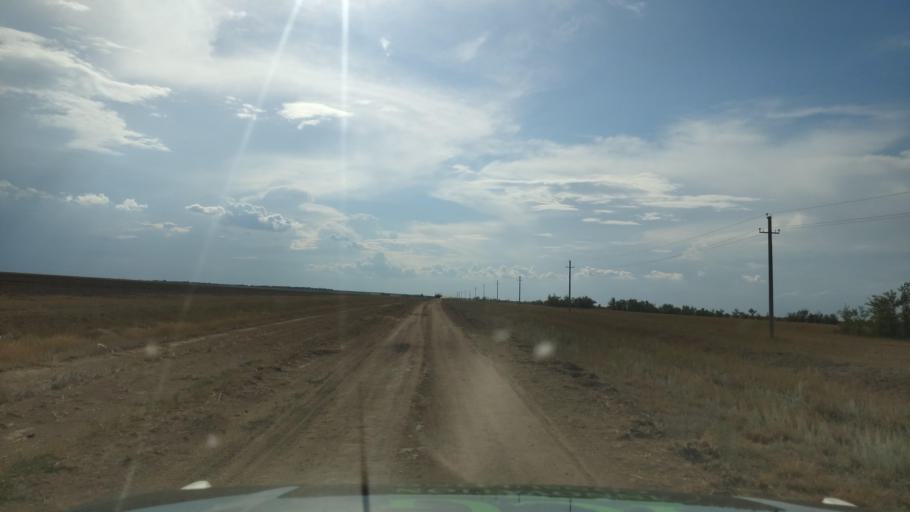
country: KZ
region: Pavlodar
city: Pavlodar
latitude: 52.5128
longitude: 77.4767
